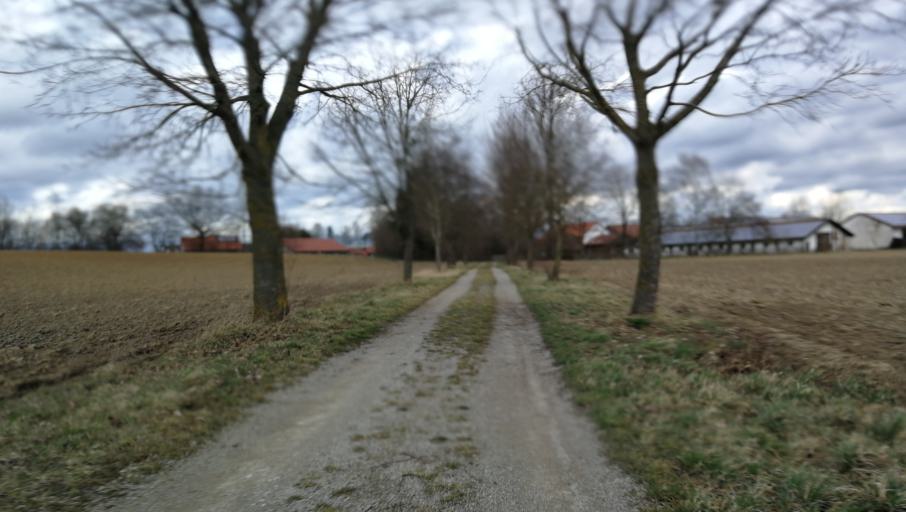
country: DE
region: Bavaria
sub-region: Upper Bavaria
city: Fuerstenfeldbruck
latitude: 48.1987
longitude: 11.2301
